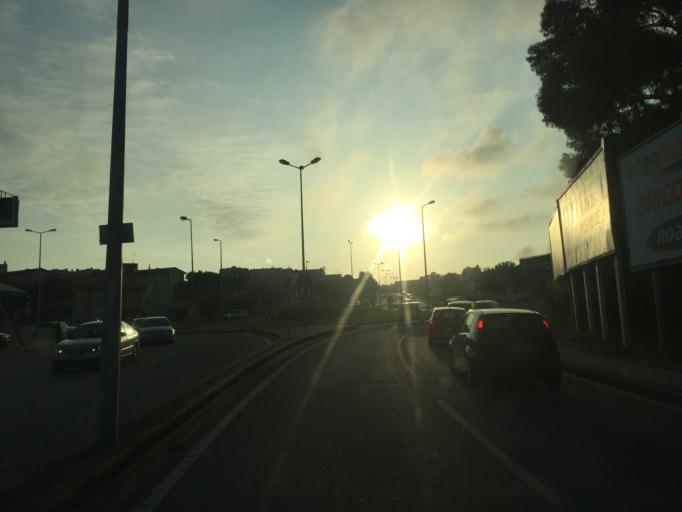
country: PT
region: Coimbra
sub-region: Figueira da Foz
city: Tavarede
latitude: 40.1634
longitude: -8.8472
